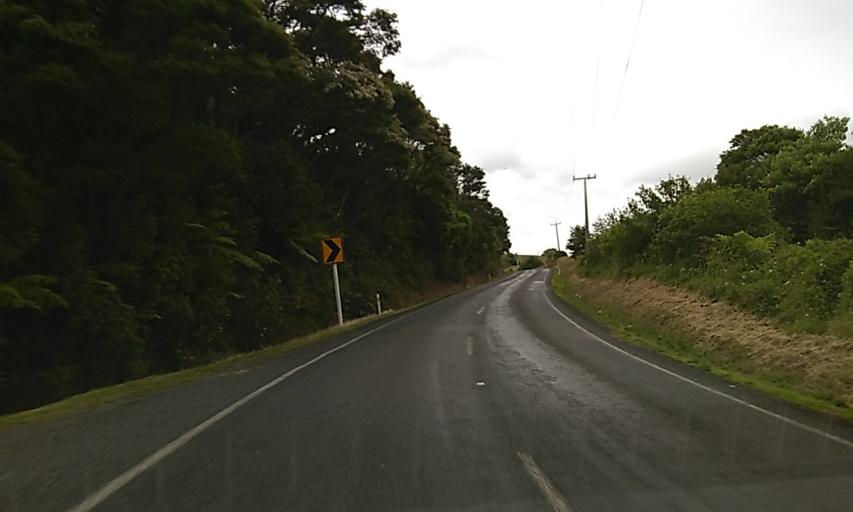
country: NZ
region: Auckland
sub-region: Auckland
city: Pukekohe East
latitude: -37.3014
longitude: 174.9383
